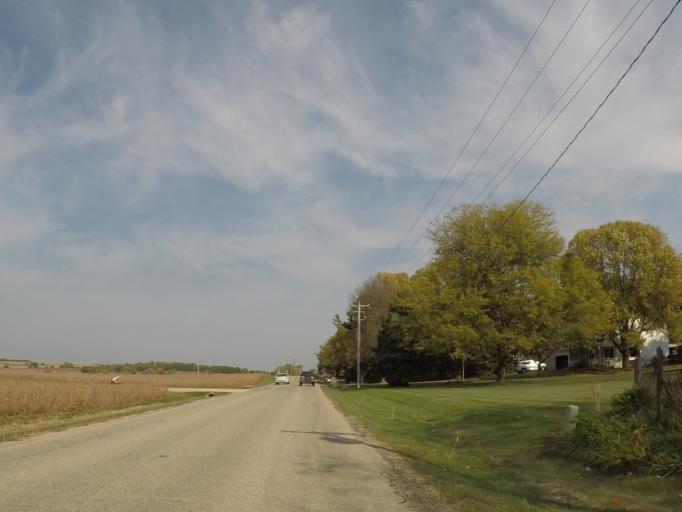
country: US
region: Wisconsin
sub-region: Dane County
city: Cross Plains
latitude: 43.0579
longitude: -89.6009
